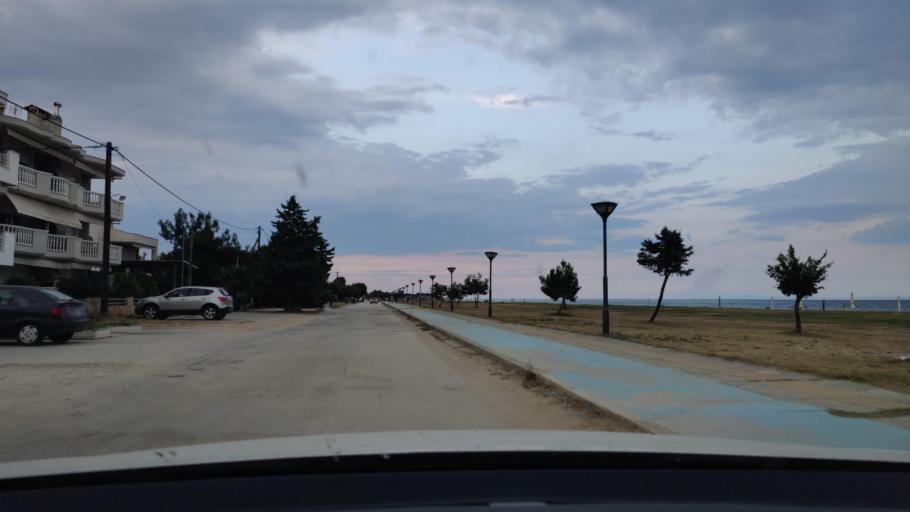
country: GR
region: East Macedonia and Thrace
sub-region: Nomos Kavalas
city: Paralia Ofryniou
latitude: 40.7709
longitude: 23.8881
